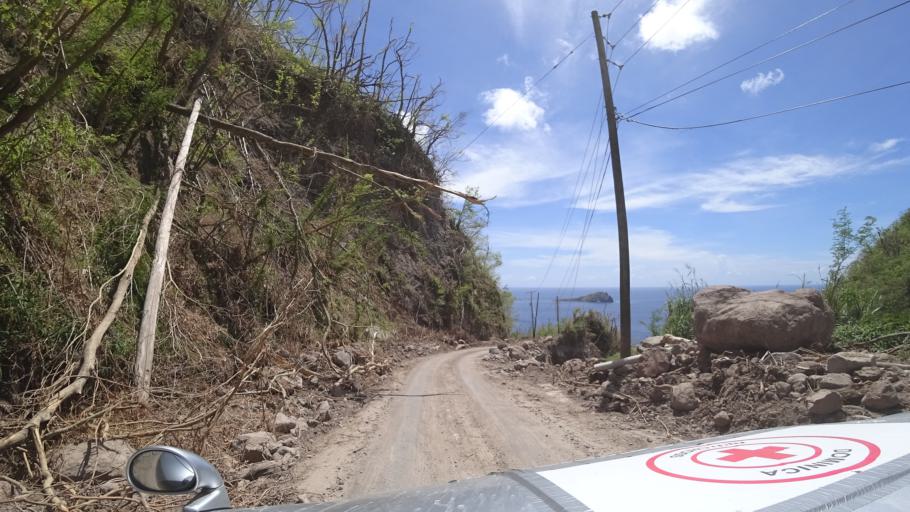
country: DM
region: Saint Mark
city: Soufriere
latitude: 15.2368
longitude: -61.3643
